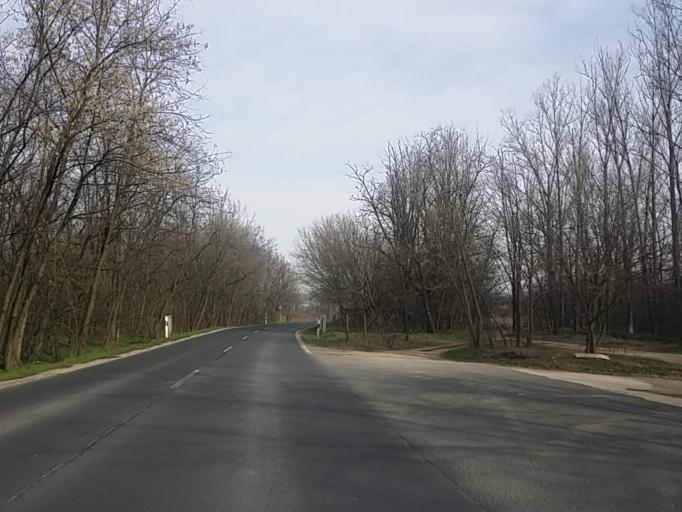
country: HU
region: Pest
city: Fot
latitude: 47.6290
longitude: 19.1994
